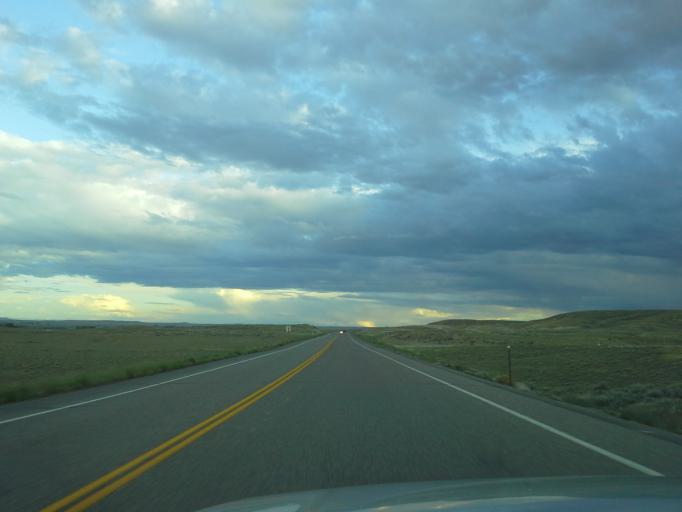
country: US
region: Wyoming
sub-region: Big Horn County
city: Basin
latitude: 44.3412
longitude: -108.0493
